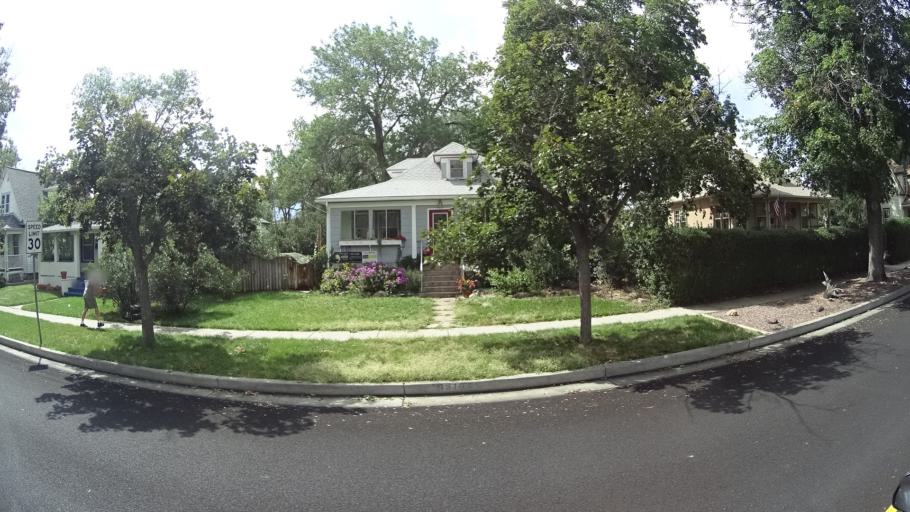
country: US
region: Colorado
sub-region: El Paso County
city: Colorado Springs
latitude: 38.8521
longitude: -104.8123
